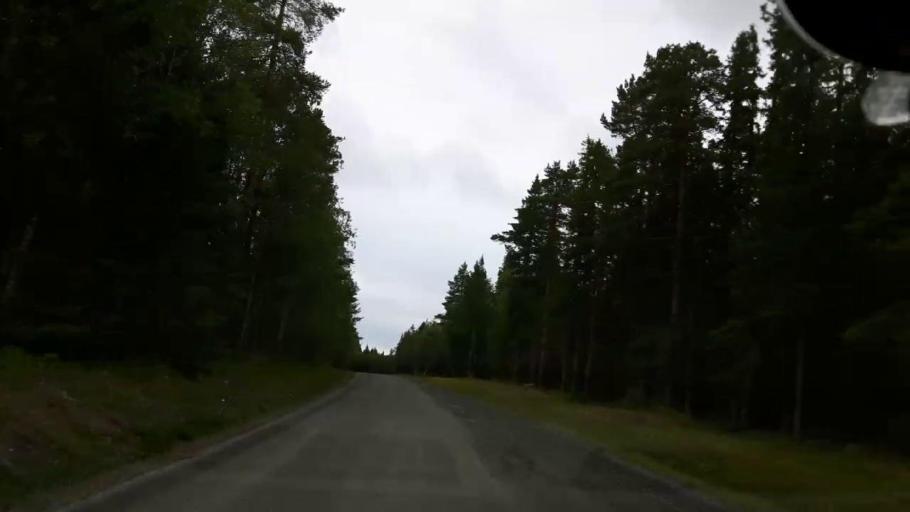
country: SE
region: Jaemtland
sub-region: OEstersunds Kommun
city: Ostersund
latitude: 63.1177
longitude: 14.5427
